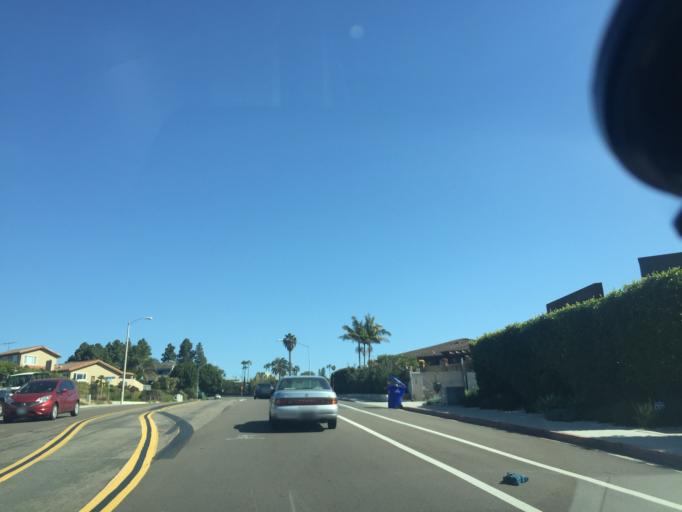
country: US
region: California
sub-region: San Diego County
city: San Diego
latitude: 32.7906
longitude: -117.1996
